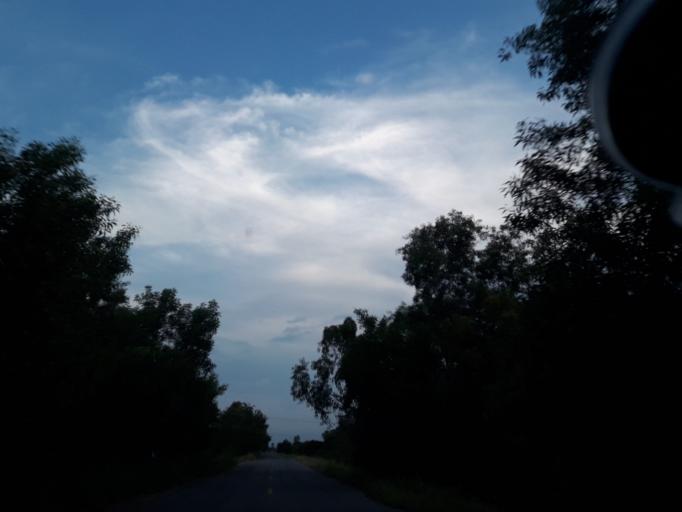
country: TH
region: Pathum Thani
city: Nong Suea
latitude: 14.2214
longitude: 100.8688
